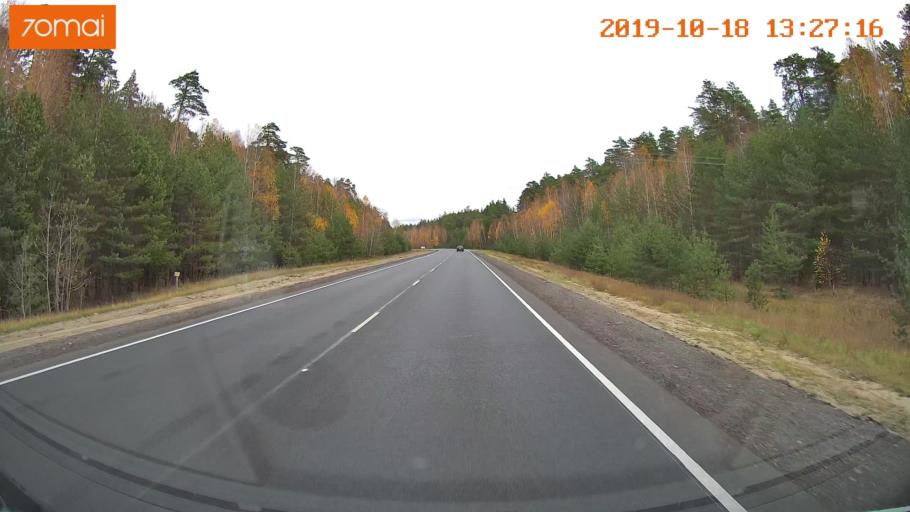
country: RU
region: Rjazan
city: Solotcha
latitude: 54.7621
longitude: 39.8519
